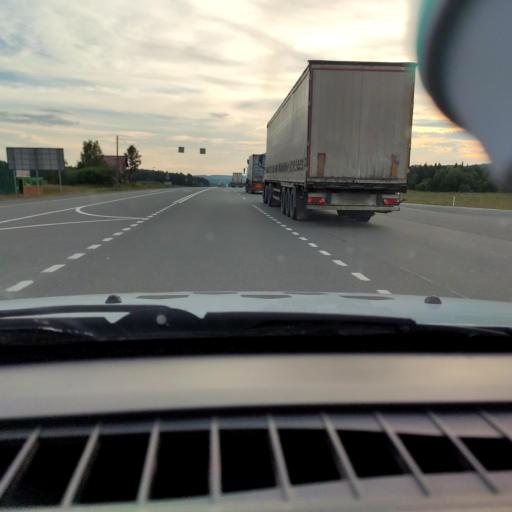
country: RU
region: Sverdlovsk
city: Bisert'
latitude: 56.7973
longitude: 58.6875
